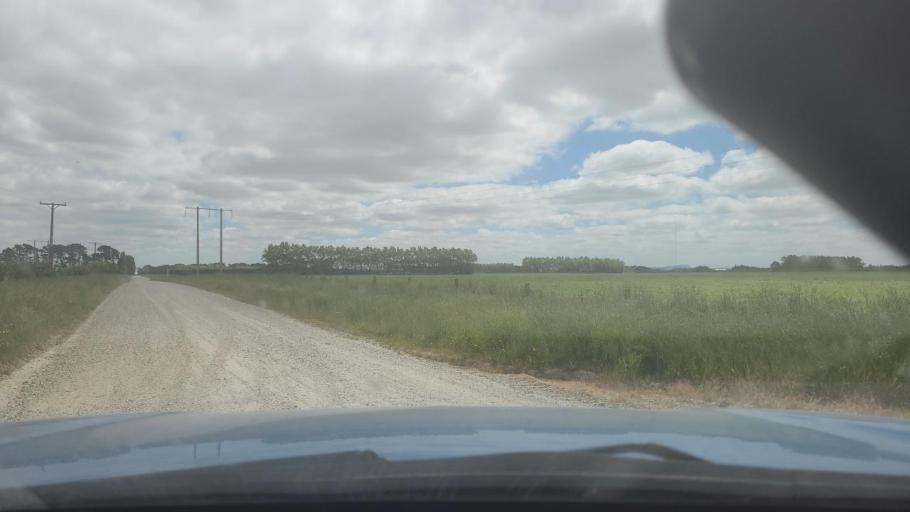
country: NZ
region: Southland
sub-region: Invercargill City
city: Invercargill
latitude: -46.3304
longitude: 168.6379
